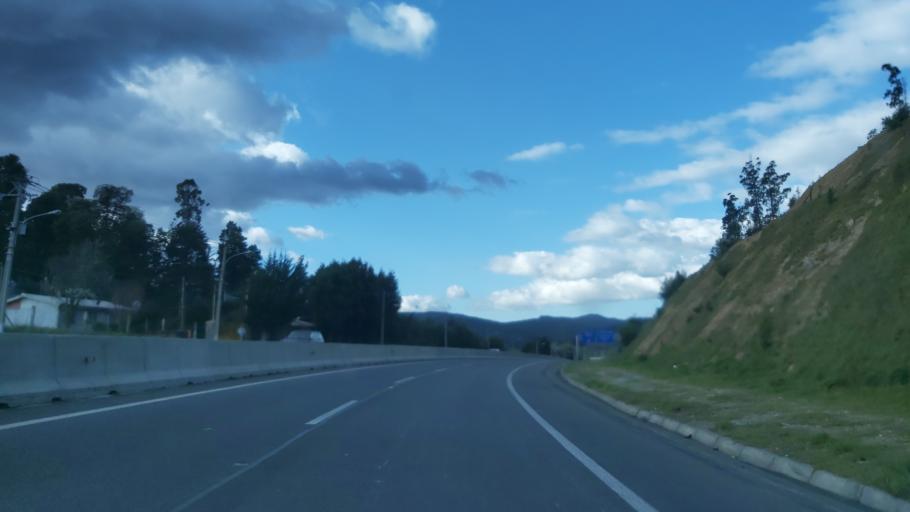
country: CL
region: Biobio
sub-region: Provincia de Concepcion
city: Penco
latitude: -36.8037
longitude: -72.9700
